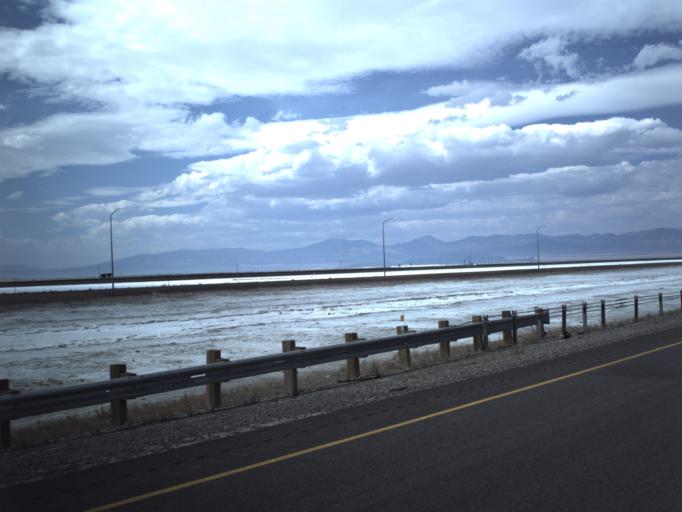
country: US
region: Utah
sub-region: Tooele County
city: Wendover
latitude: 40.7396
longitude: -113.8593
